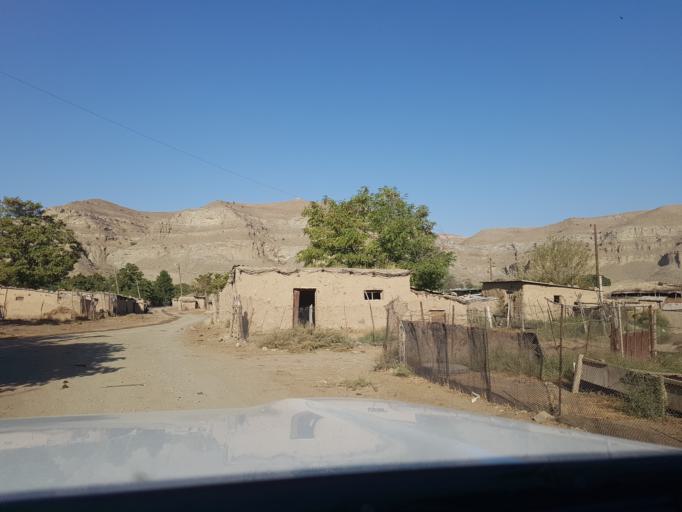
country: TM
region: Balkan
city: Magtymguly
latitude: 38.3011
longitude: 56.7469
